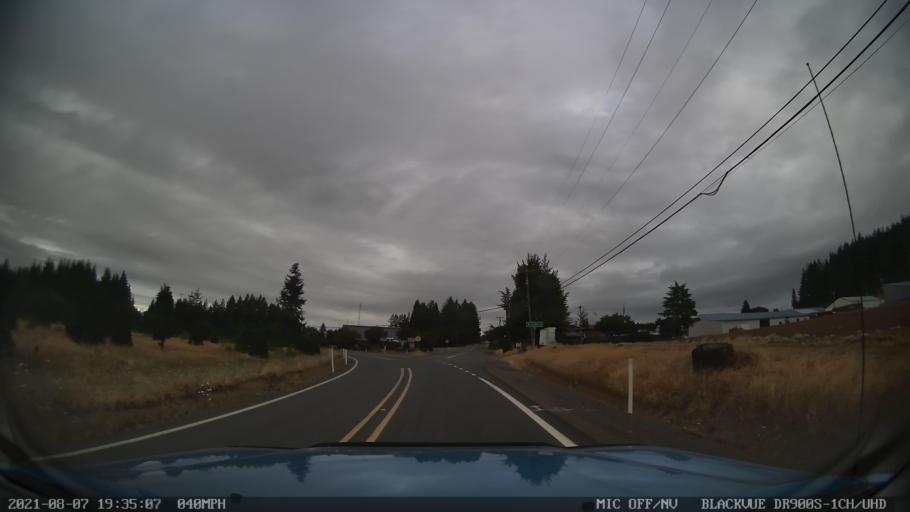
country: US
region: Oregon
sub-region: Marion County
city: Silverton
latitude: 44.9251
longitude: -122.6567
